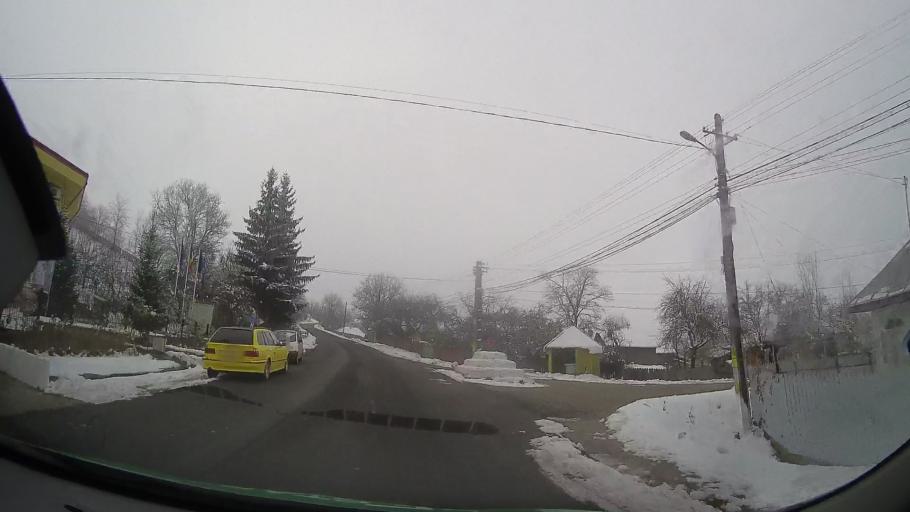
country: RO
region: Bacau
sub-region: Comuna Oncesti
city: Oncesti
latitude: 46.4716
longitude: 27.2558
